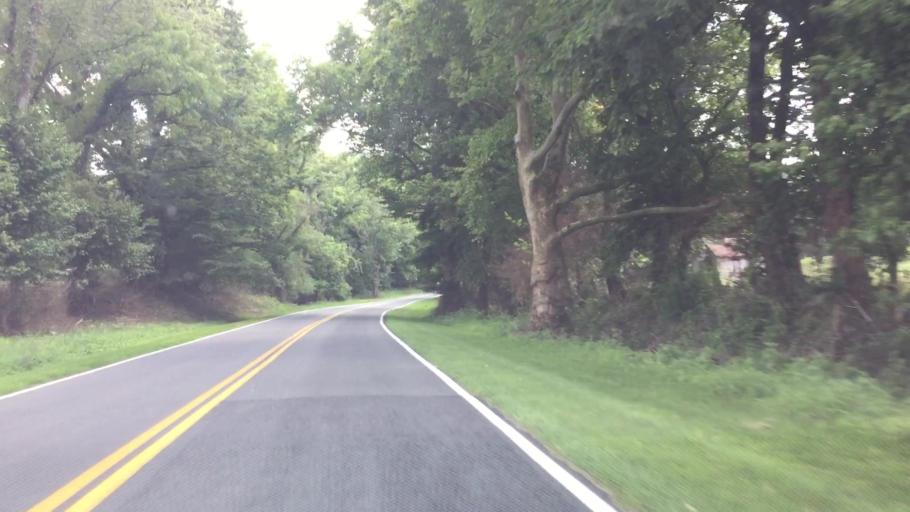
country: US
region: Virginia
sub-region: Pulaski County
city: Pulaski
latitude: 36.9979
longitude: -80.7997
